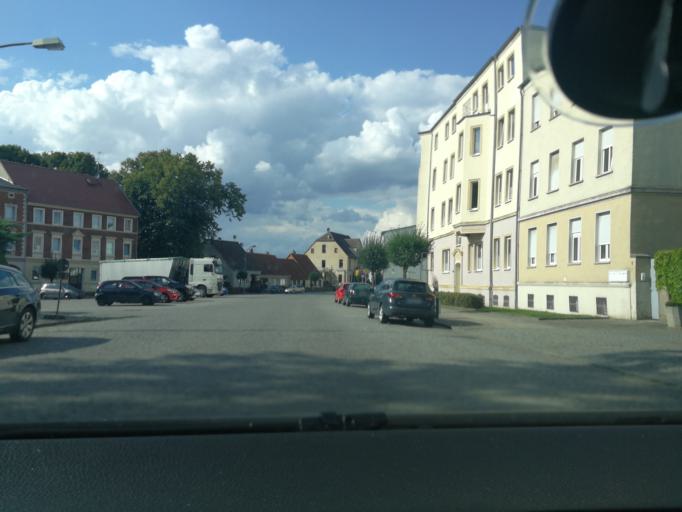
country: DE
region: Brandenburg
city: Pritzwalk
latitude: 53.1471
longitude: 12.1846
